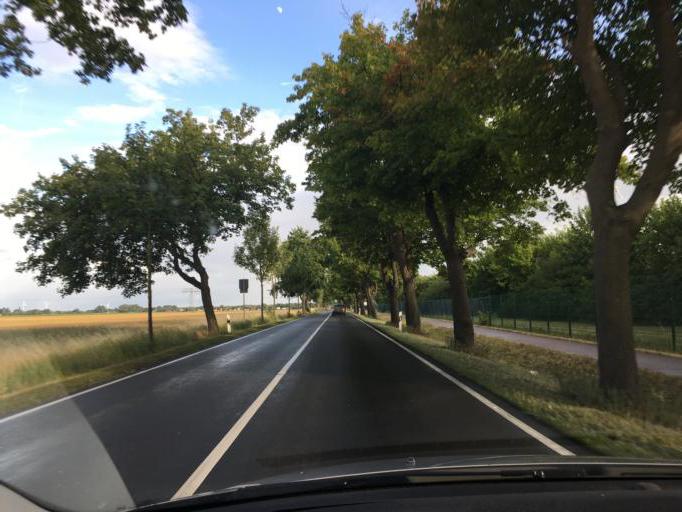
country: DE
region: Saxony-Anhalt
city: Weissandt-Golzau
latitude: 51.6718
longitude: 12.0845
